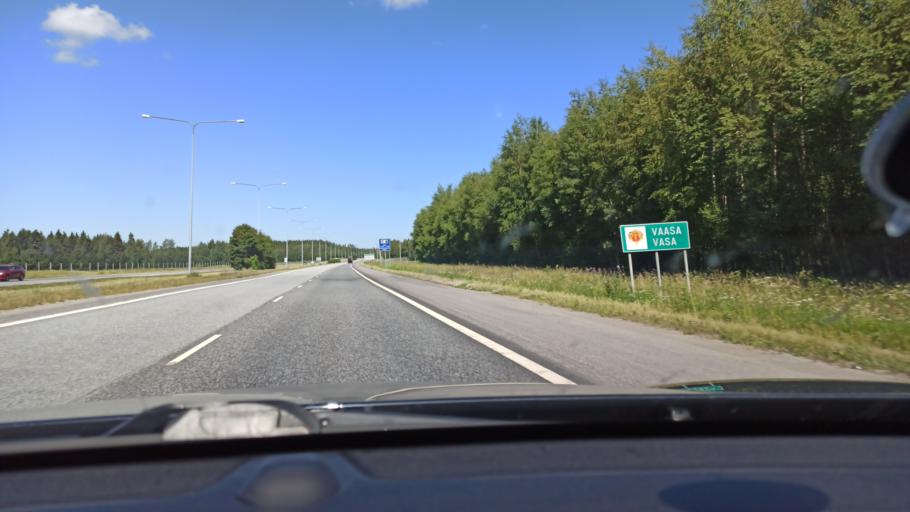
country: FI
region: Ostrobothnia
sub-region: Vaasa
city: Ristinummi
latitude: 63.0432
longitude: 21.7273
